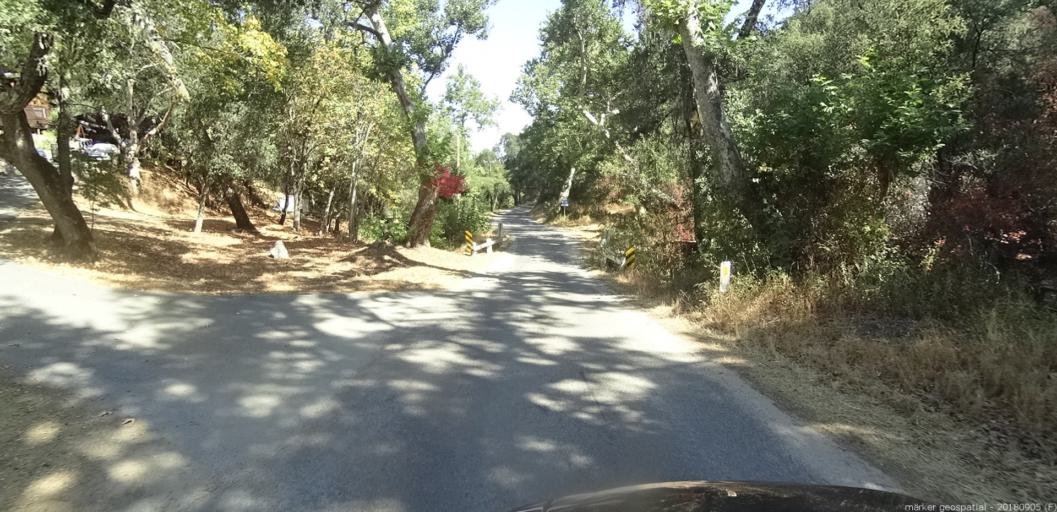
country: US
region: California
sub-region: Monterey County
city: Gonzales
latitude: 36.3704
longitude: -121.5907
